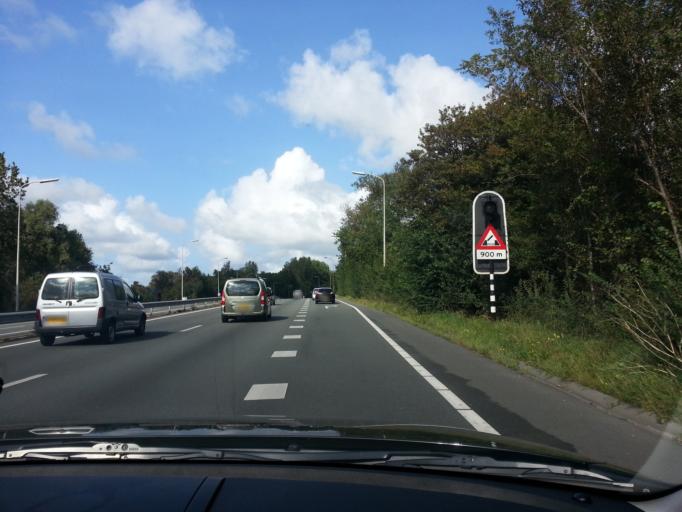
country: NL
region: South Holland
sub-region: Gemeente Katwijk
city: Katwijk aan den Rijn
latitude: 52.1938
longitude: 4.4198
